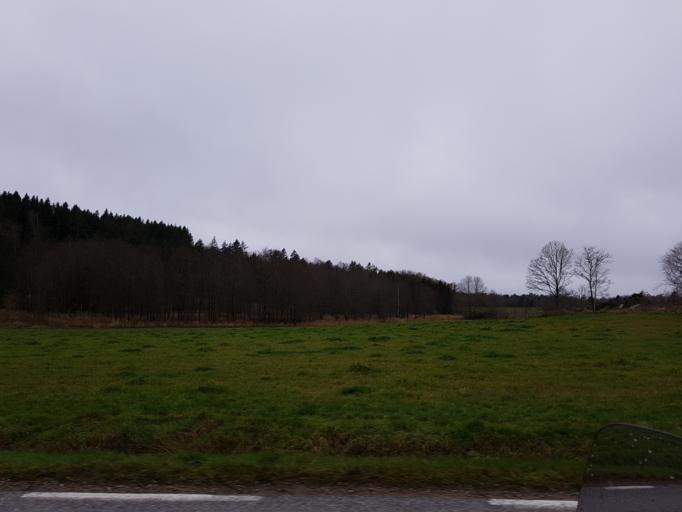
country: SE
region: Vaestra Goetaland
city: Svanesund
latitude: 58.1606
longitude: 11.7731
